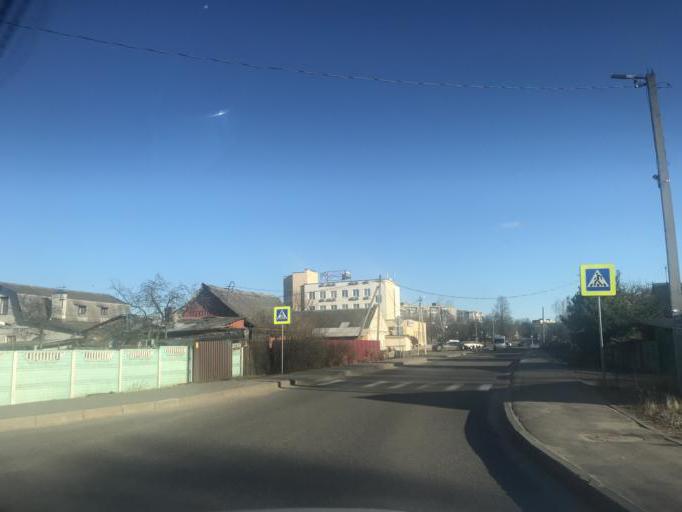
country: BY
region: Mogilev
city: Mahilyow
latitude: 53.9102
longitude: 30.3559
